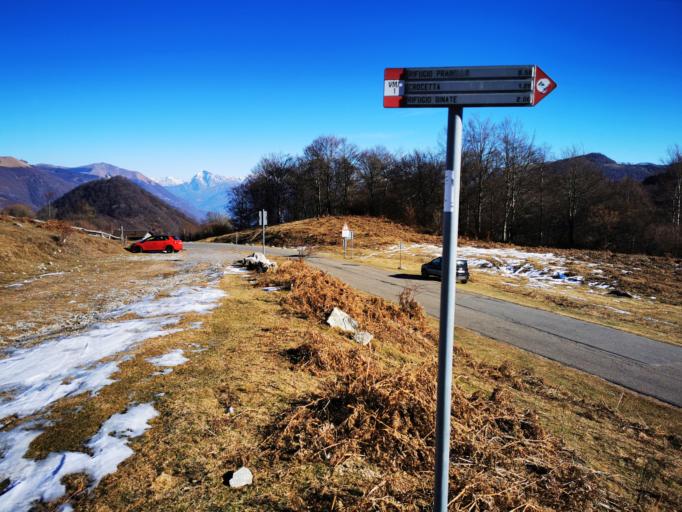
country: IT
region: Lombardy
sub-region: Provincia di Como
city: Casasco Intelvi
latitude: 45.9209
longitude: 9.0717
